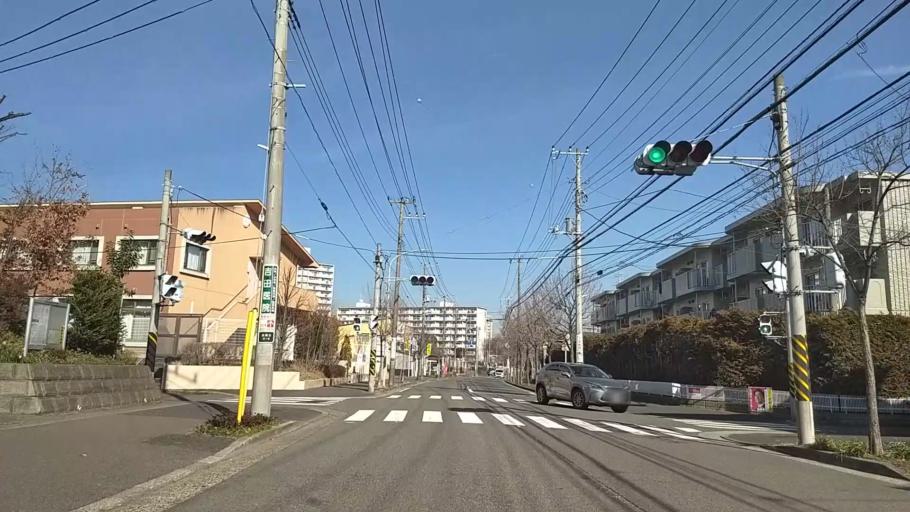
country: JP
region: Kanagawa
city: Kamakura
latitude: 35.3719
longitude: 139.5872
